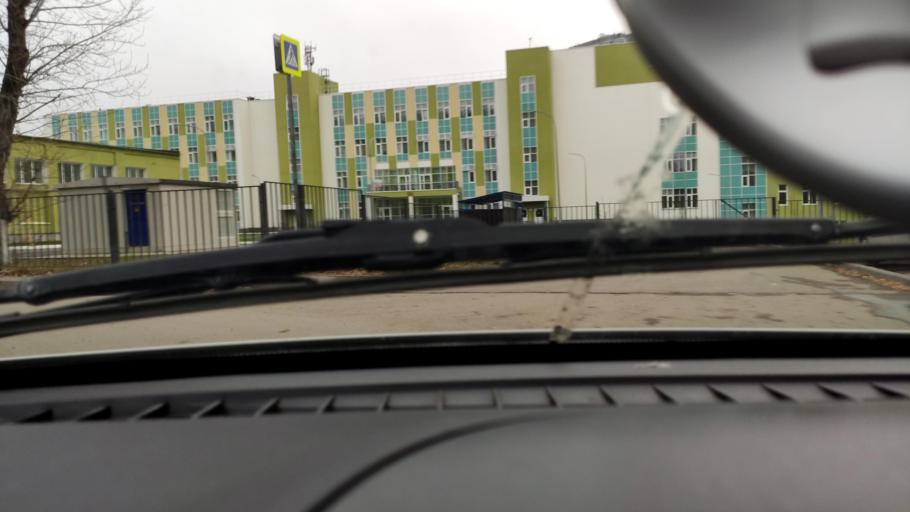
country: RU
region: Perm
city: Perm
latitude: 57.9933
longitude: 56.2432
